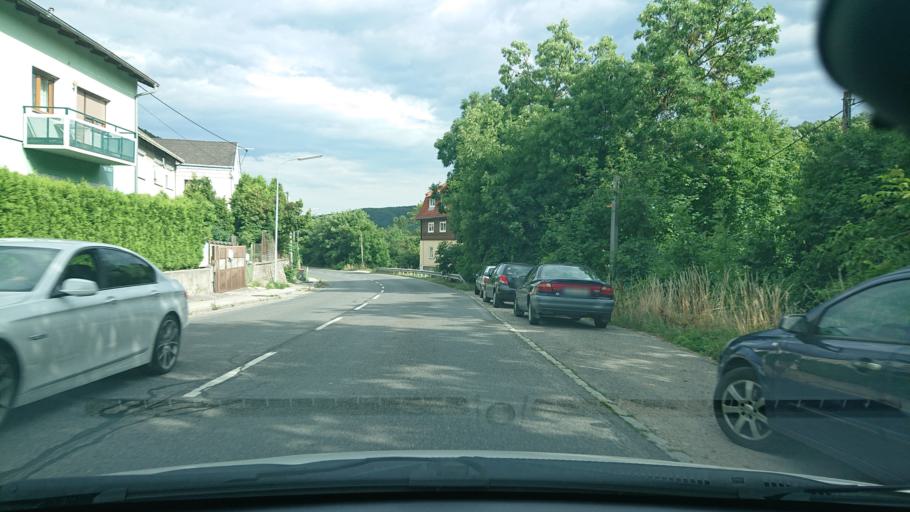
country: AT
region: Lower Austria
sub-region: Politischer Bezirk Baden
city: Berndorf
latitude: 47.9430
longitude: 16.1326
